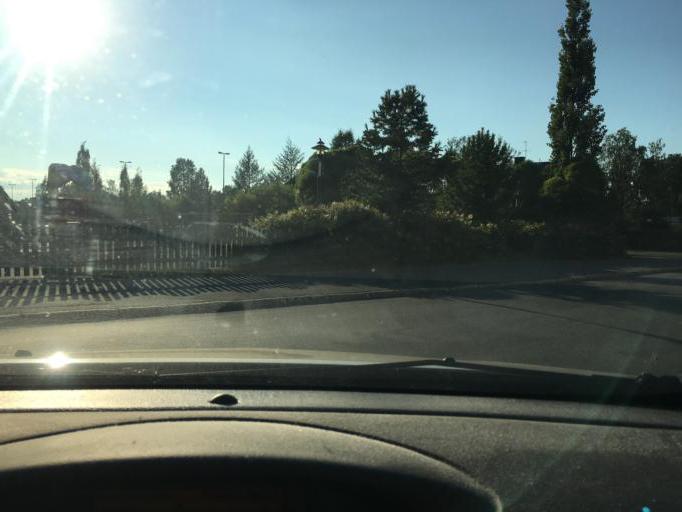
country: SE
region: Norrbotten
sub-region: Bodens Kommun
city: Boden
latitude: 65.8252
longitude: 21.6814
